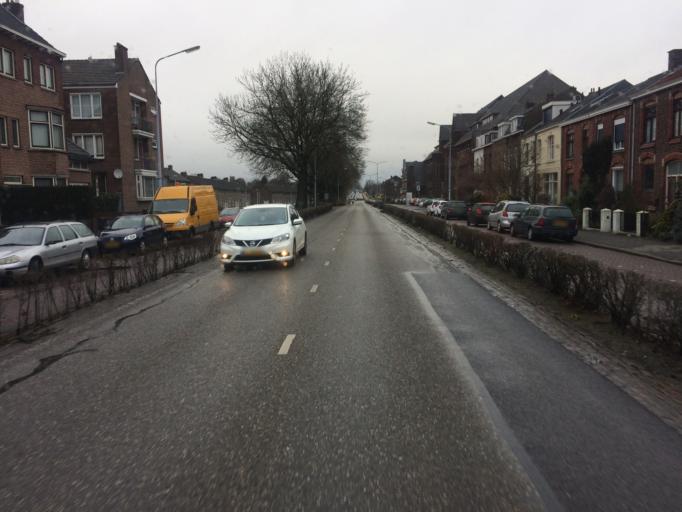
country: NL
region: Limburg
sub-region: Gemeente Maastricht
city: Maastricht
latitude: 50.8528
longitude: 5.6714
